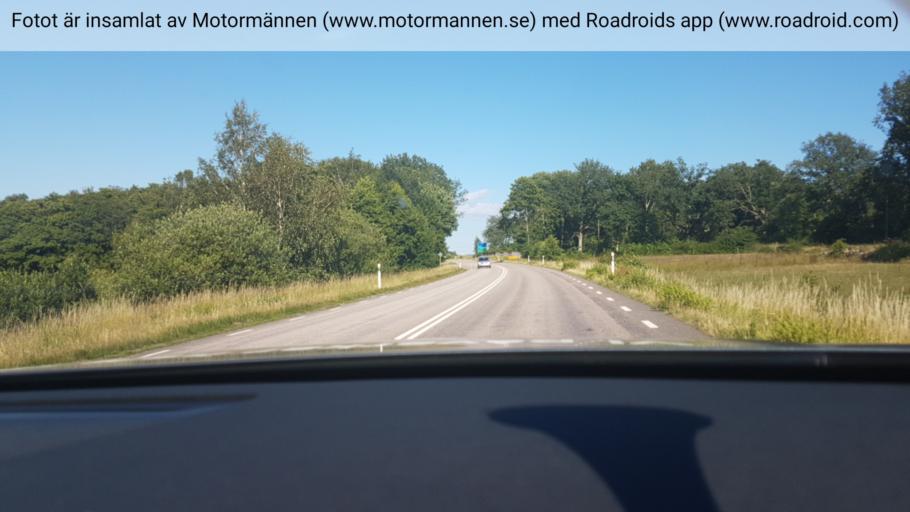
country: SE
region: Halland
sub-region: Falkenbergs Kommun
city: Falkenberg
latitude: 56.8992
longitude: 12.5680
